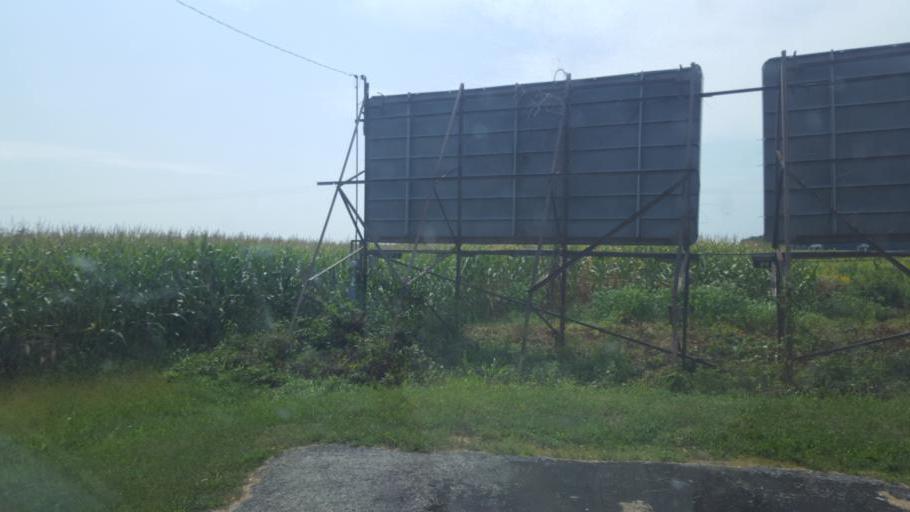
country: US
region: Ohio
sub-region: Marion County
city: Marion
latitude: 40.5101
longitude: -83.0741
